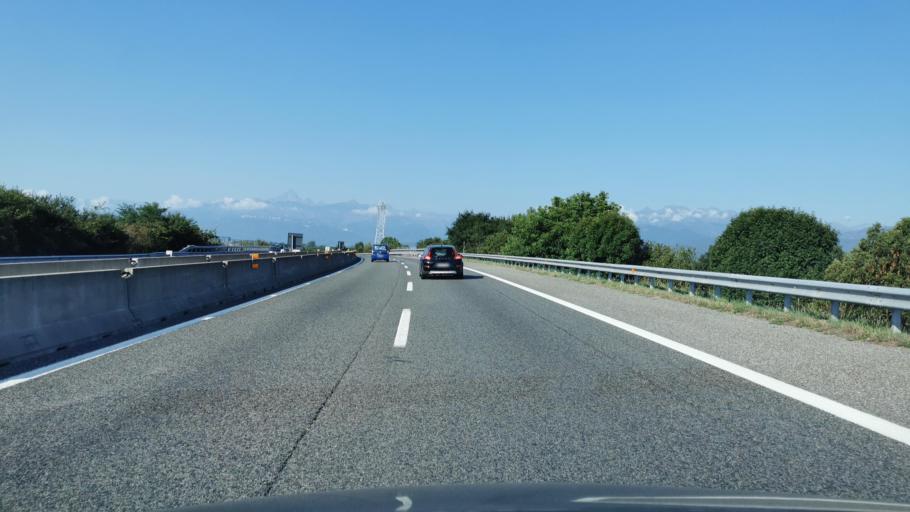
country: IT
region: Piedmont
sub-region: Provincia di Torino
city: Airasca
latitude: 44.9252
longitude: 7.4585
